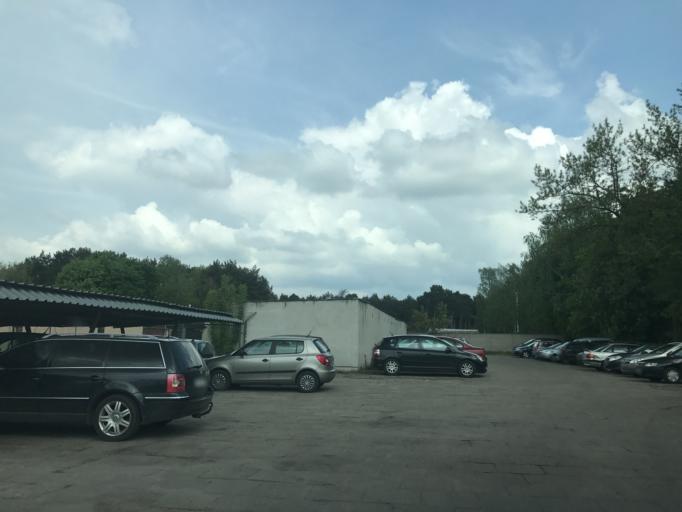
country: PL
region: Kujawsko-Pomorskie
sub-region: Bydgoszcz
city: Bydgoszcz
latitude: 53.1456
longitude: 18.0114
